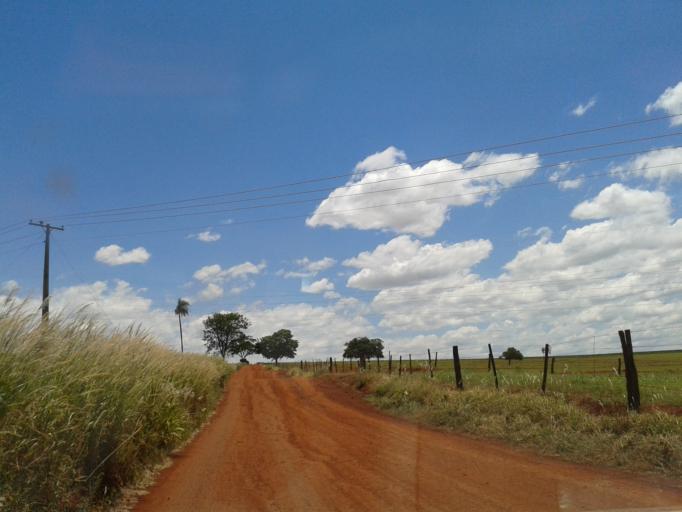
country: BR
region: Minas Gerais
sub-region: Centralina
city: Centralina
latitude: -18.7064
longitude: -49.2159
